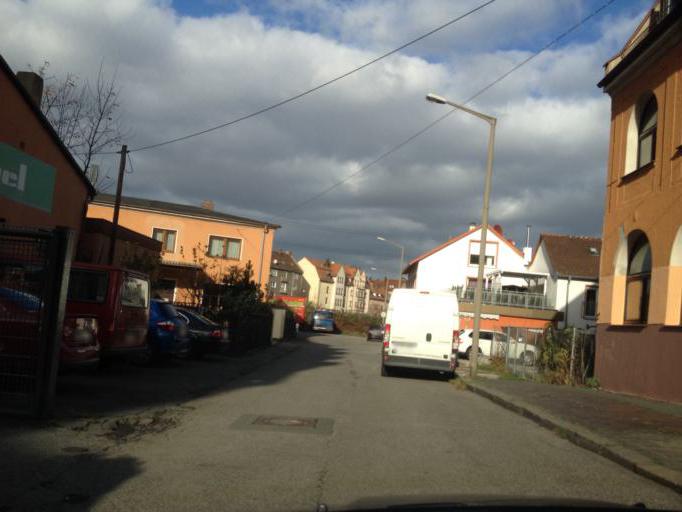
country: DE
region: Bavaria
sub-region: Regierungsbezirk Mittelfranken
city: Grossreuth bei Schweinau
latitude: 49.4352
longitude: 11.0507
